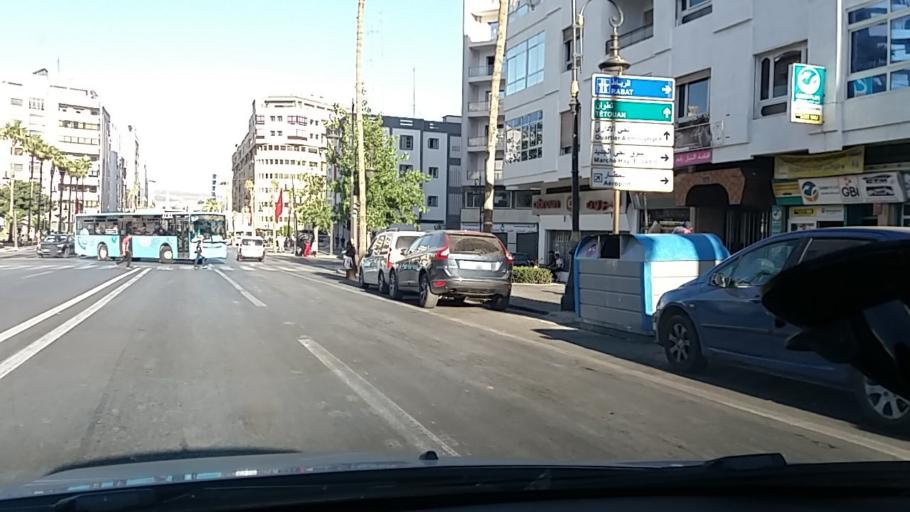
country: MA
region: Tanger-Tetouan
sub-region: Tanger-Assilah
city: Tangier
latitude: 35.7705
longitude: -5.8098
